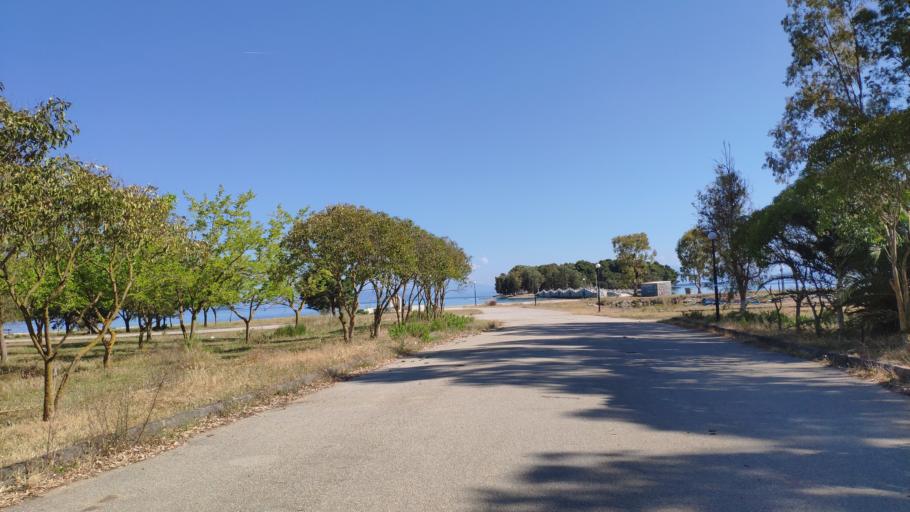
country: GR
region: West Greece
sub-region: Nomos Aitolias kai Akarnanias
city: Vonitsa
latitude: 38.9210
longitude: 20.9002
